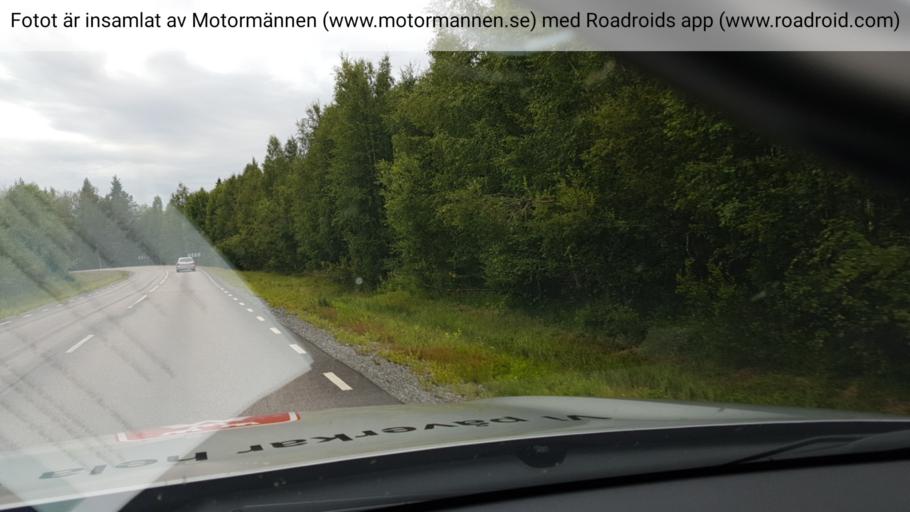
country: SE
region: Norrbotten
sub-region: Lulea Kommun
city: Gammelstad
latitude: 65.6608
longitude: 22.0600
